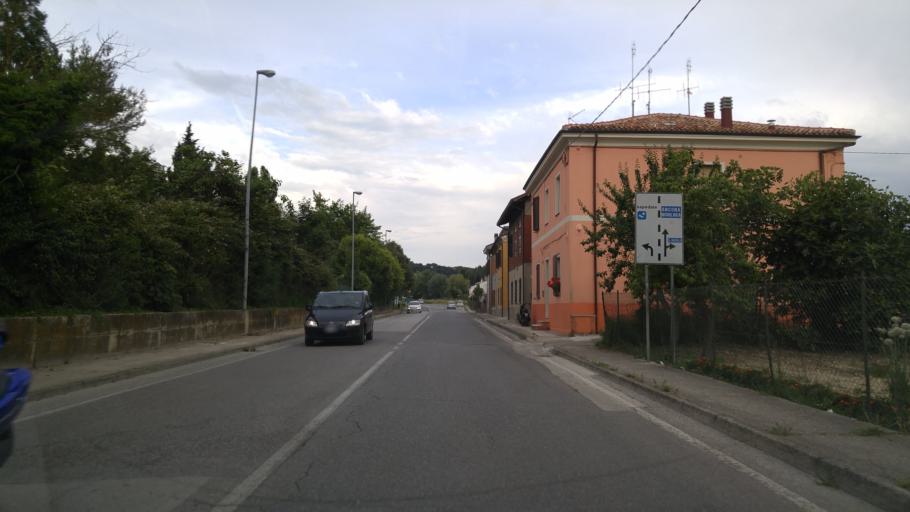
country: IT
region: The Marches
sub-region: Provincia di Pesaro e Urbino
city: Pesaro
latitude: 43.8898
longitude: 12.9264
